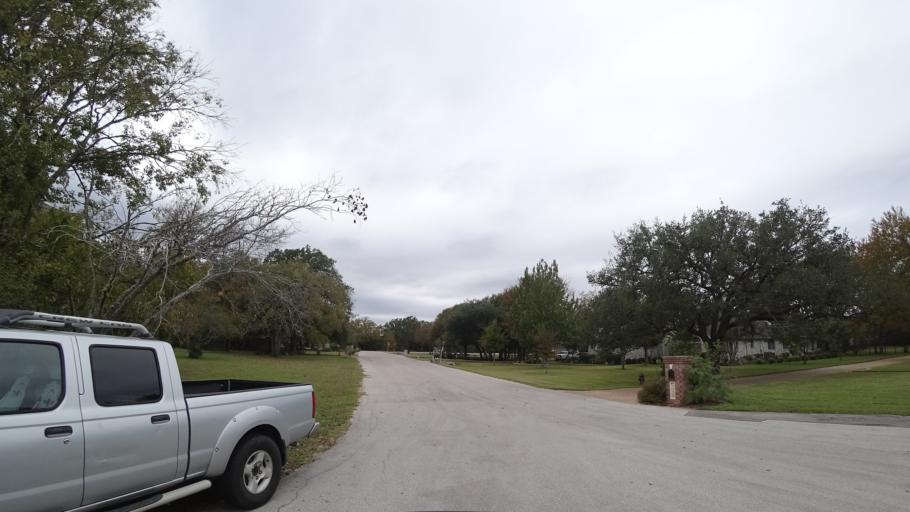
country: US
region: Texas
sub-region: Travis County
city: Shady Hollow
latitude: 30.1591
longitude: -97.8721
